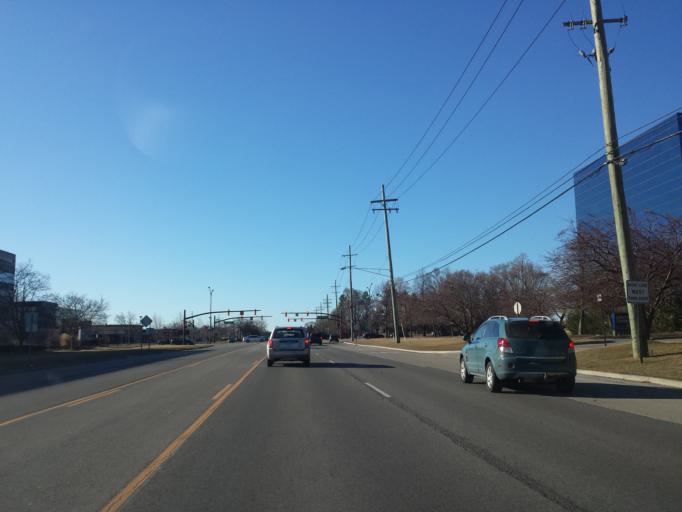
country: US
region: Michigan
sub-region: Oakland County
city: Clawson
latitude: 42.5638
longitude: -83.1478
